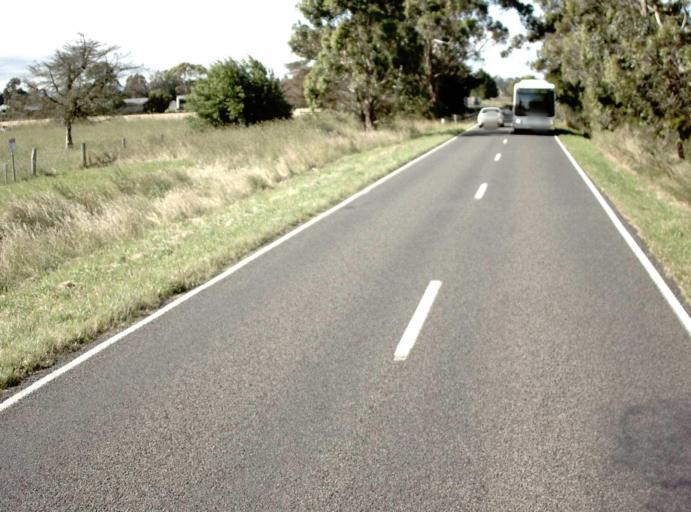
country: AU
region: Victoria
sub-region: Latrobe
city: Traralgon
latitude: -38.1570
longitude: 146.4925
